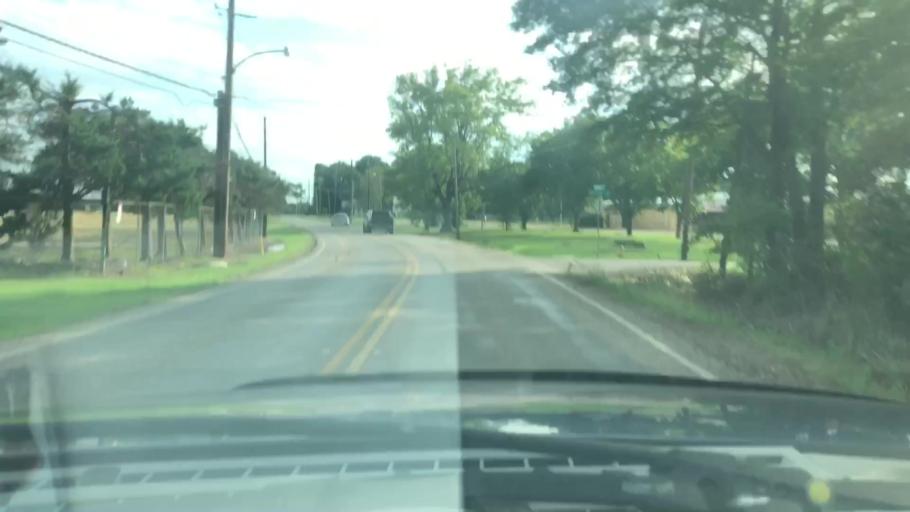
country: US
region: Texas
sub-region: Bowie County
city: Texarkana
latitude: 33.3970
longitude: -94.0643
